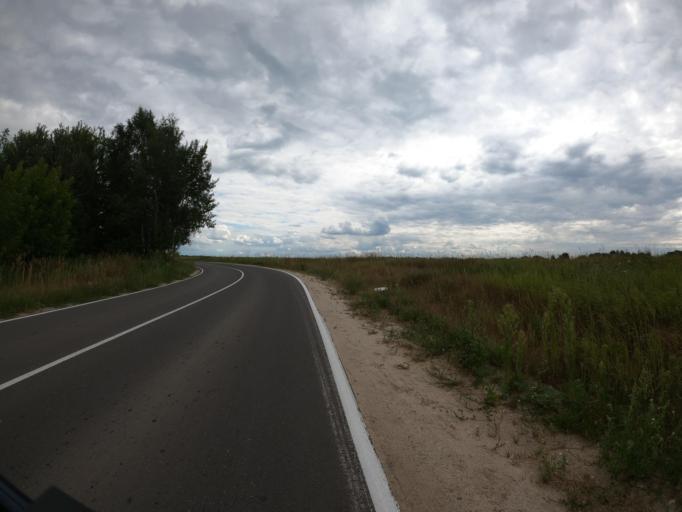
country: RU
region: Moskovskaya
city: Bronnitsy
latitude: 55.4886
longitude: 38.2421
